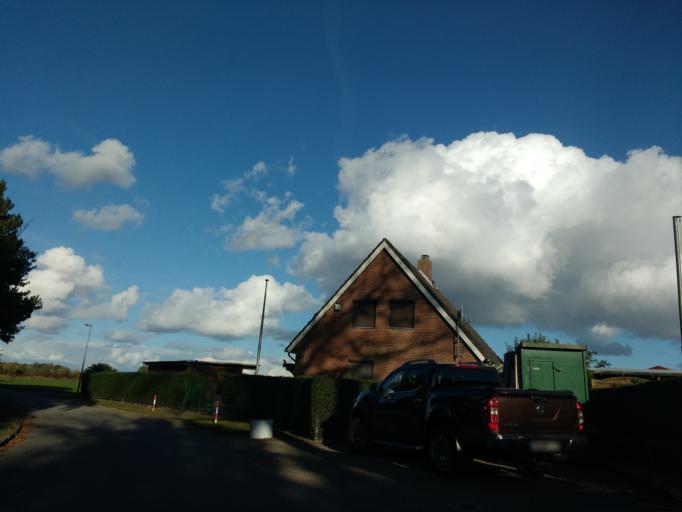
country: DE
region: Schleswig-Holstein
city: Grossenbrode
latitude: 54.4287
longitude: 11.1115
